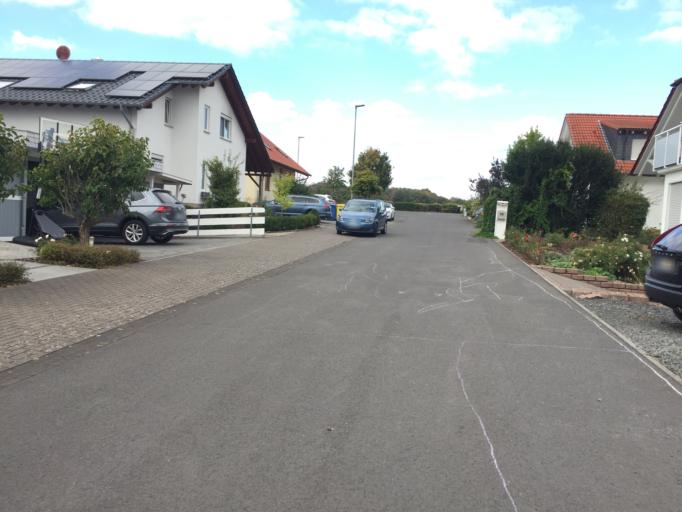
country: DE
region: Hesse
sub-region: Regierungsbezirk Giessen
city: Lich
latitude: 50.4887
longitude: 8.7979
